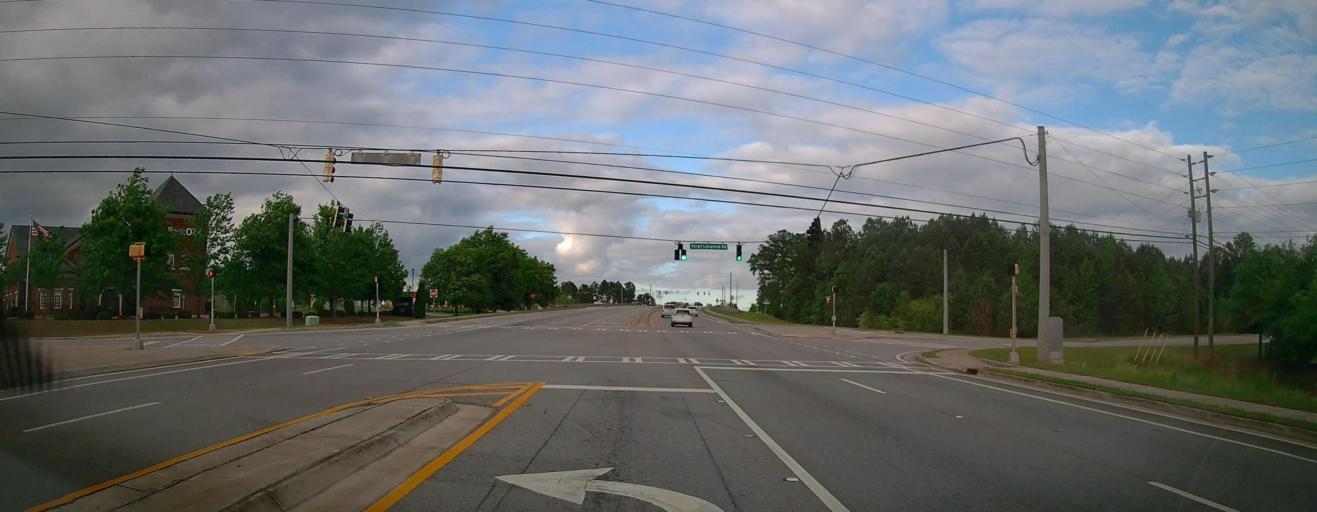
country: US
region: Georgia
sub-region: Oconee County
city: Watkinsville
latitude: 33.9133
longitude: -83.4627
